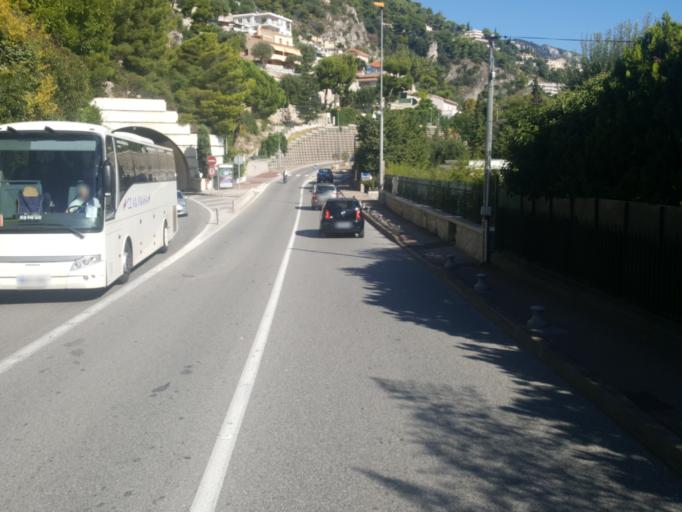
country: FR
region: Provence-Alpes-Cote d'Azur
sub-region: Departement des Alpes-Maritimes
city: Cap-d'Ail
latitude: 43.7266
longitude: 7.4072
